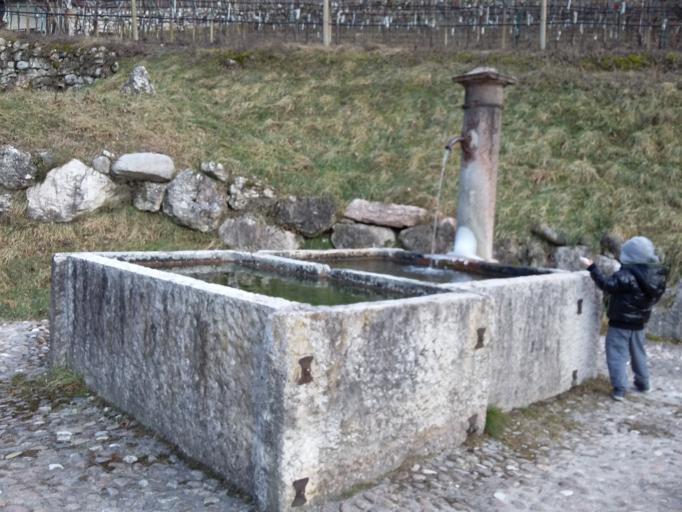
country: IT
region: Trentino-Alto Adige
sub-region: Provincia di Trento
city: Besenello
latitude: 45.9280
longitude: 11.1187
